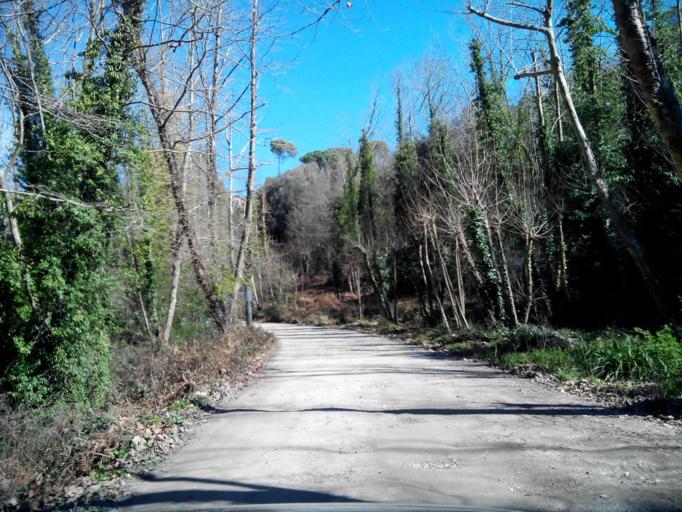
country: ES
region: Catalonia
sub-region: Provincia de Barcelona
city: Dosrius
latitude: 41.6039
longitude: 2.4550
